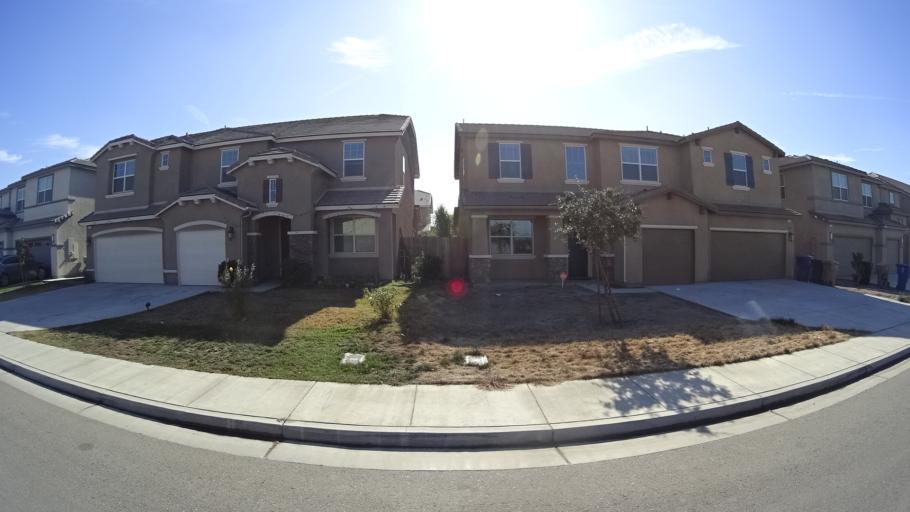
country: US
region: California
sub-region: Kern County
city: Greenfield
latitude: 35.2875
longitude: -119.0590
